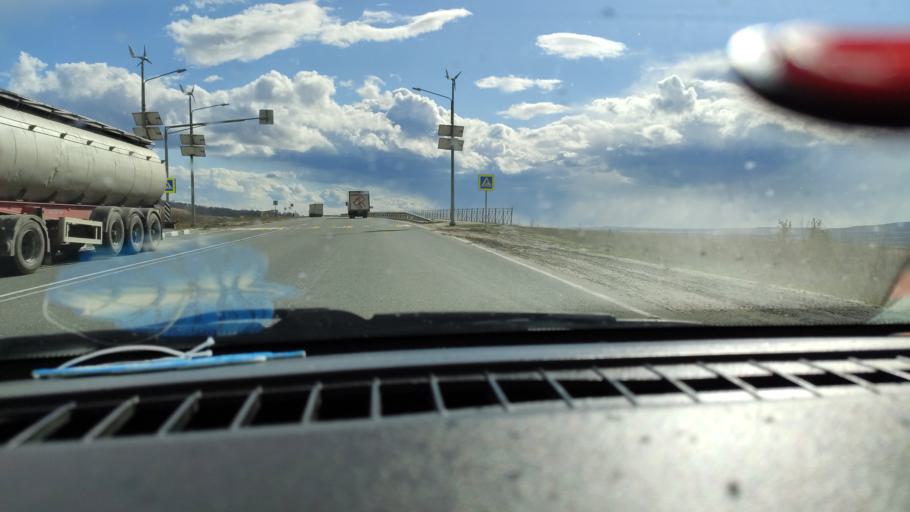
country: RU
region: Saratov
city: Alekseyevka
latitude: 52.3443
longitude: 47.9362
